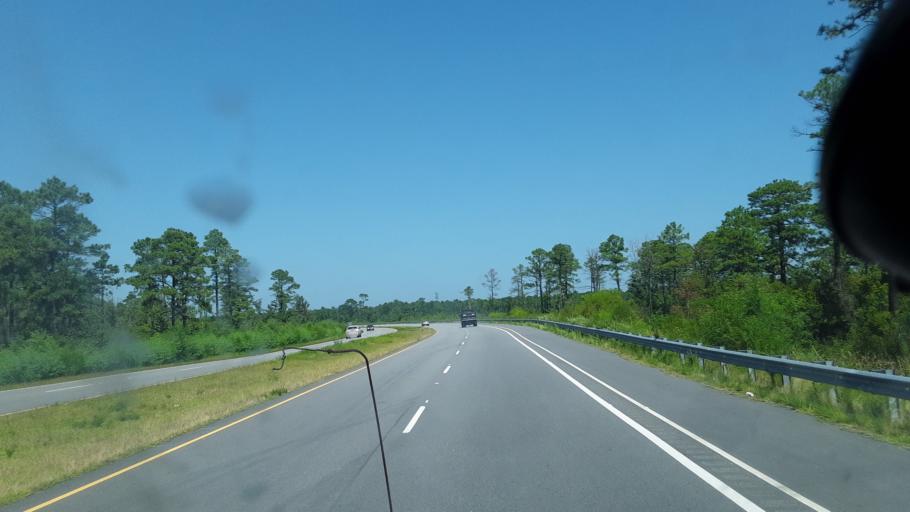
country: US
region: South Carolina
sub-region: Horry County
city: Forestbrook
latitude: 33.7986
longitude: -78.8829
